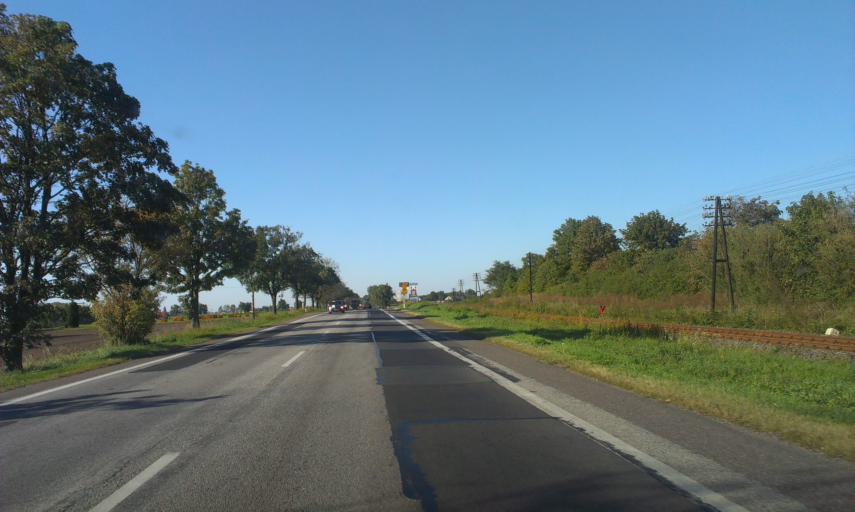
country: PL
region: Kujawsko-Pomorskie
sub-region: Powiat torunski
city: Chelmza
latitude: 53.1417
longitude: 18.6180
